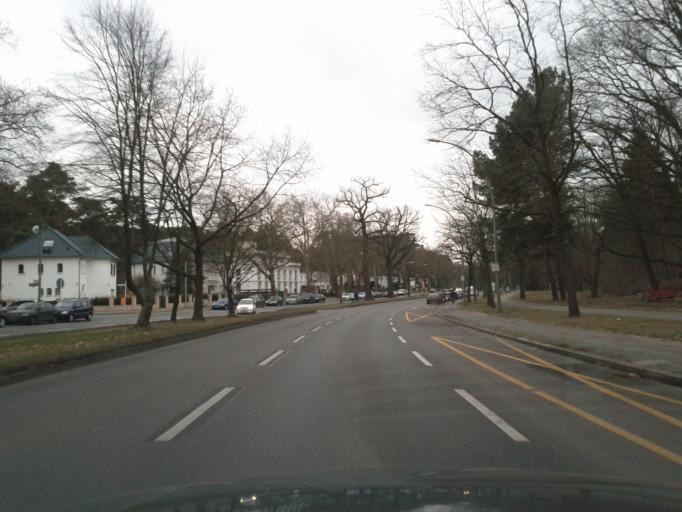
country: DE
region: Berlin
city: Dahlem
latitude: 52.4666
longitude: 13.2782
